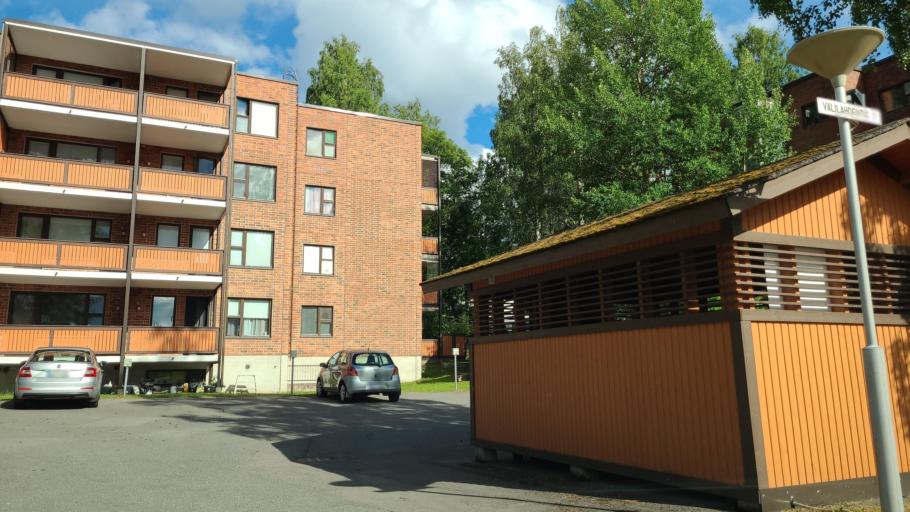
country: FI
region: Northern Savo
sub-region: Kuopio
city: Kuopio
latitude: 62.9273
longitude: 27.6305
